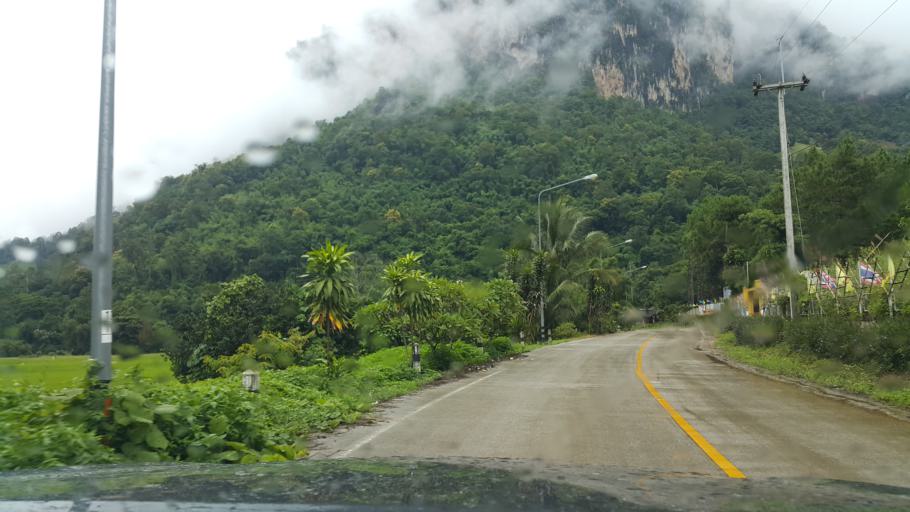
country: TH
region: Phayao
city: Chiang Kham
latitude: 19.4999
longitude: 100.4536
